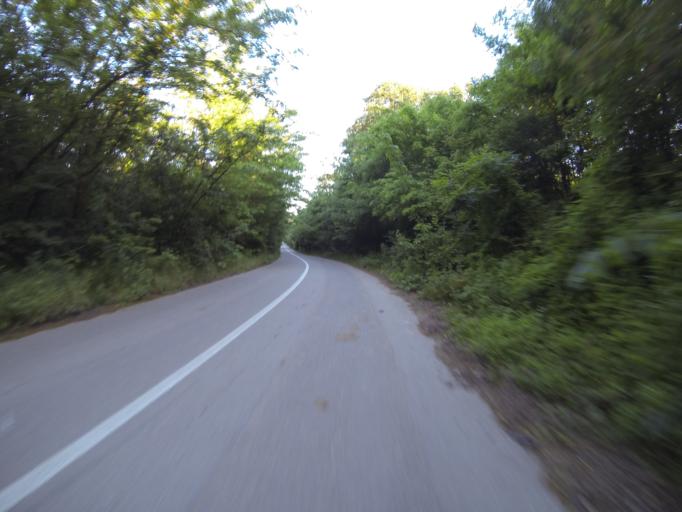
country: RO
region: Dolj
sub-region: Comuna Tuglui
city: Tuglui
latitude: 44.1750
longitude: 23.8167
